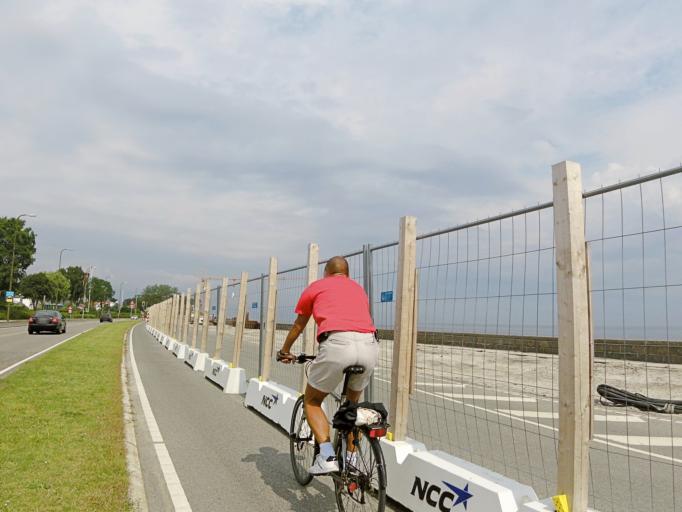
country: DK
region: Capital Region
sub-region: Gentofte Kommune
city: Charlottenlund
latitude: 55.7671
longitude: 12.5968
